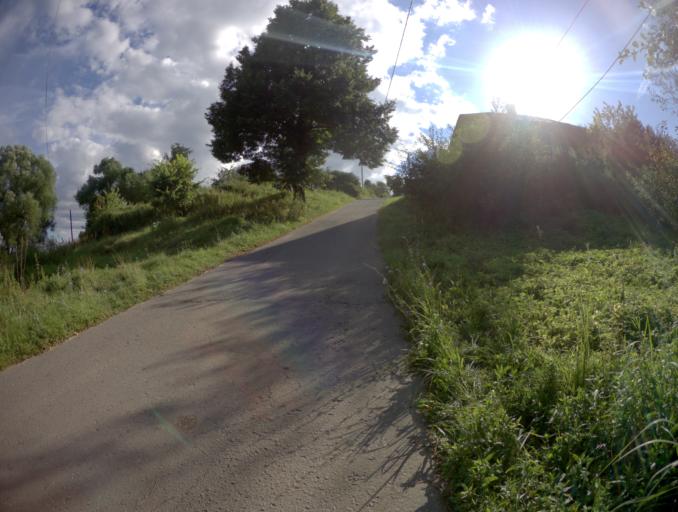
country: RU
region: Vladimir
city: Vladimir
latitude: 56.1180
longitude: 40.3921
